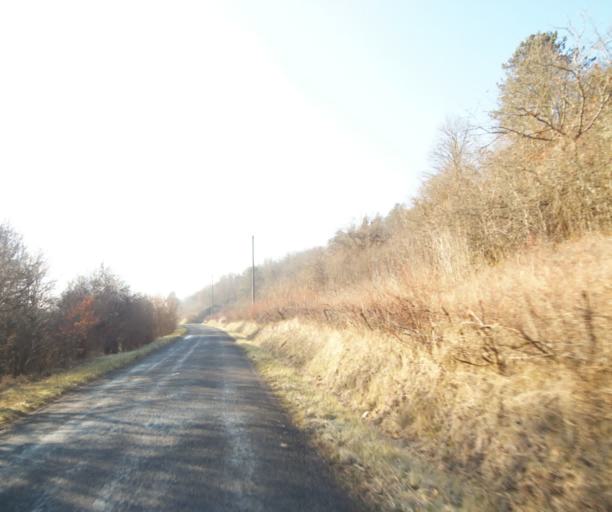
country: FR
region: Champagne-Ardenne
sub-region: Departement de la Haute-Marne
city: Chevillon
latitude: 48.5028
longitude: 5.1649
